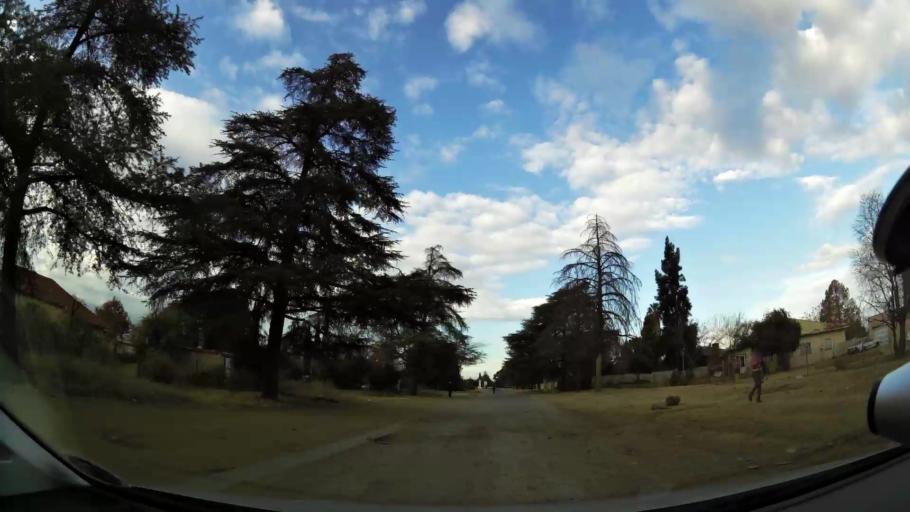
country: ZA
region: Orange Free State
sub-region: Lejweleputswa District Municipality
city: Welkom
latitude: -27.9918
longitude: 26.7099
